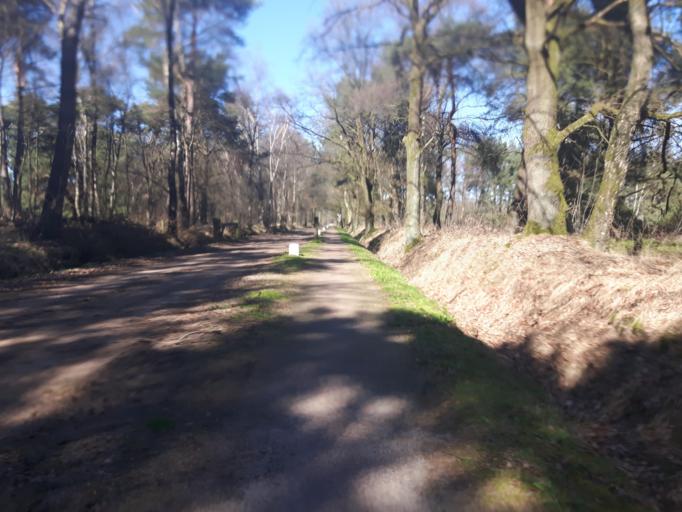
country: NL
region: Overijssel
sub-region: Gemeente Enschede
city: Enschede
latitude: 52.1728
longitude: 6.8234
